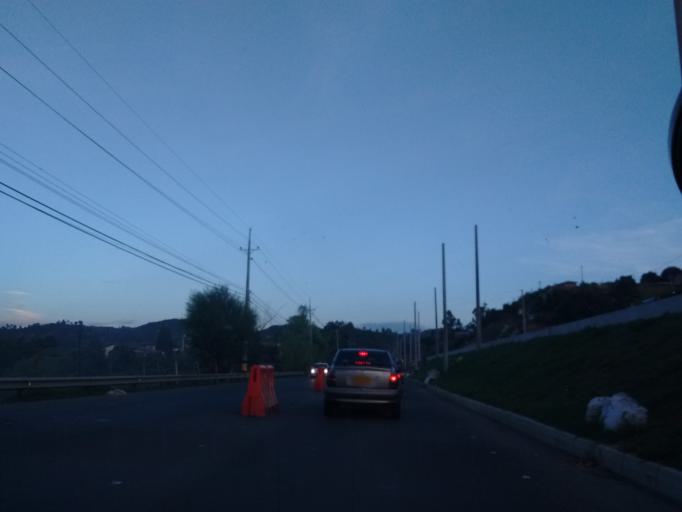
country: CO
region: Antioquia
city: Santuario
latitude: 6.1397
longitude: -75.2983
